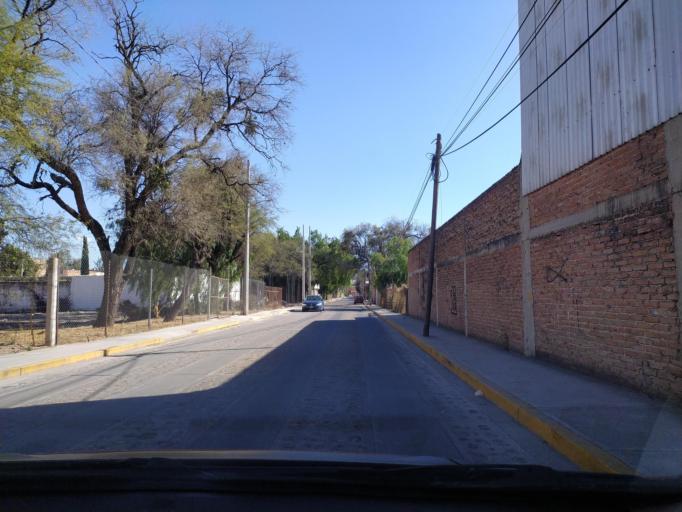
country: MX
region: Guanajuato
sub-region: San Francisco del Rincon
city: Estacion de San Francisco
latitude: 21.0267
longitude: -101.8326
